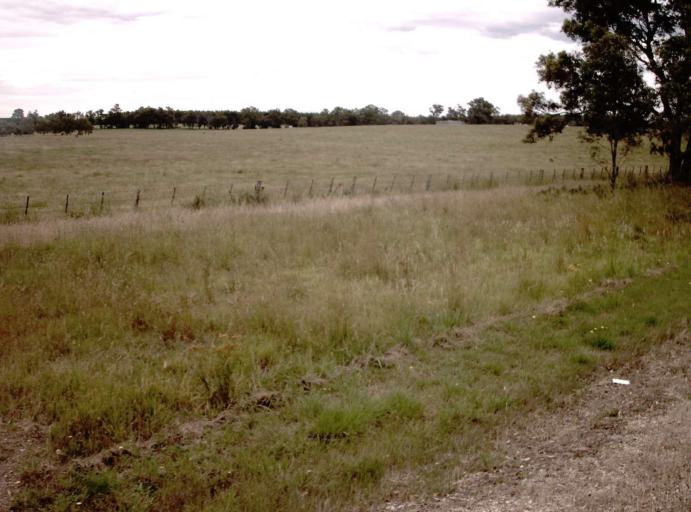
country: AU
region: Victoria
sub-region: East Gippsland
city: Bairnsdale
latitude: -37.7979
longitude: 147.3376
